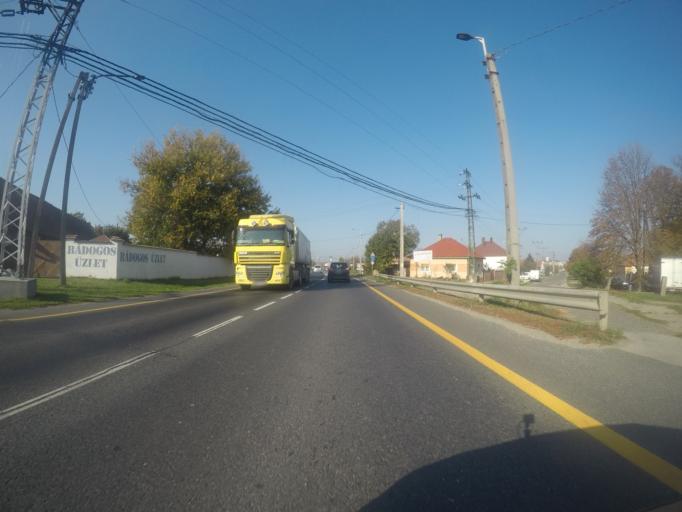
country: HU
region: Tolna
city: Dunafoldvar
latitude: 46.8002
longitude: 18.9180
